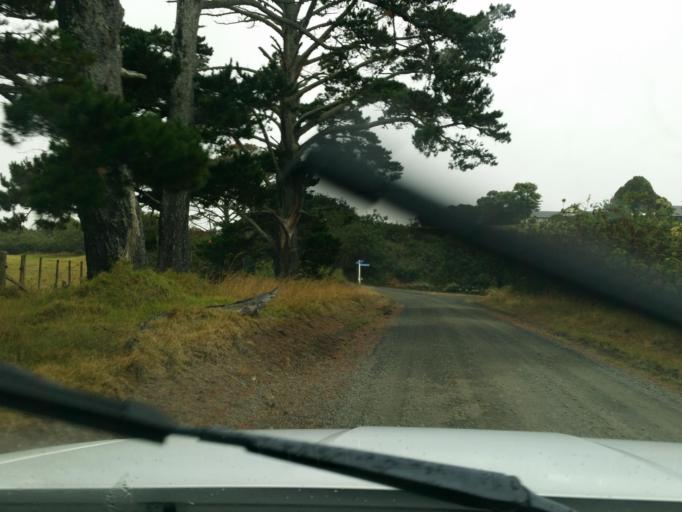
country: NZ
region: Northland
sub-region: Kaipara District
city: Dargaville
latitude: -36.0752
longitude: 173.8896
